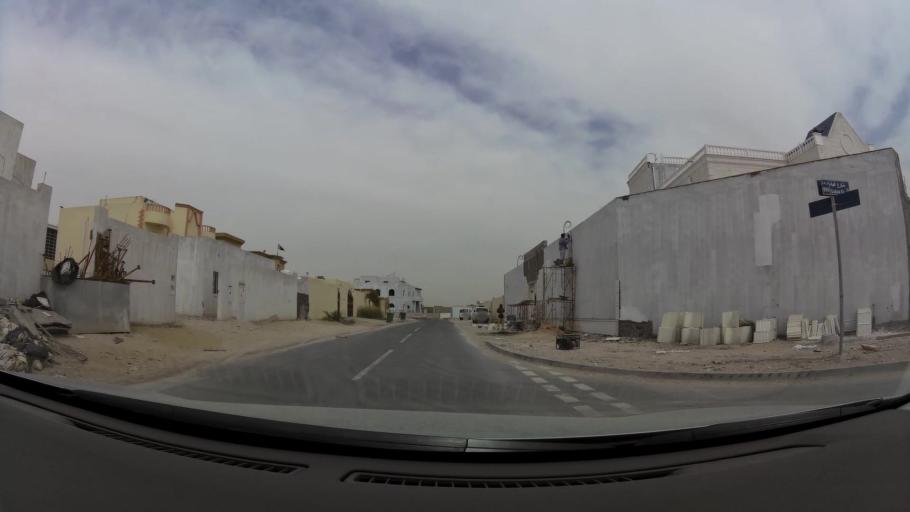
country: QA
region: Al Wakrah
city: Al Wukayr
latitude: 25.1975
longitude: 51.4541
